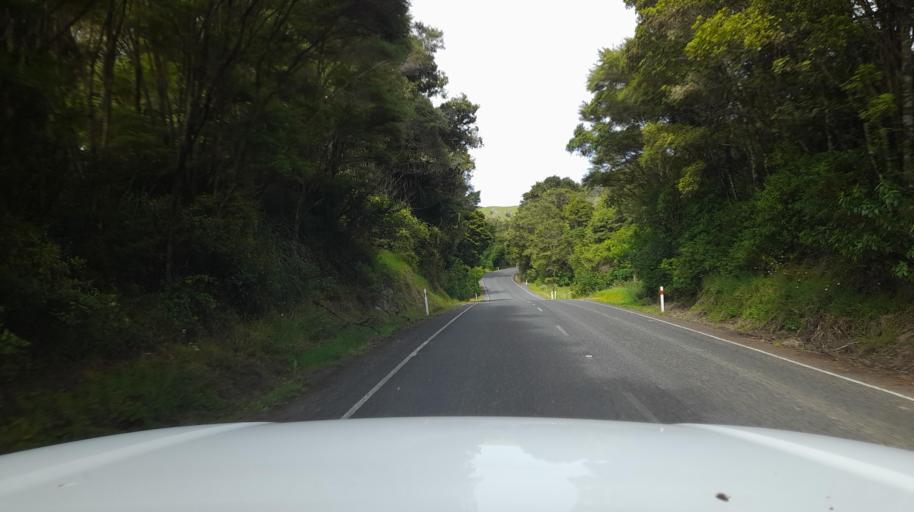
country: NZ
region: Northland
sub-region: Far North District
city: Taipa
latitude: -35.2566
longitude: 173.5338
